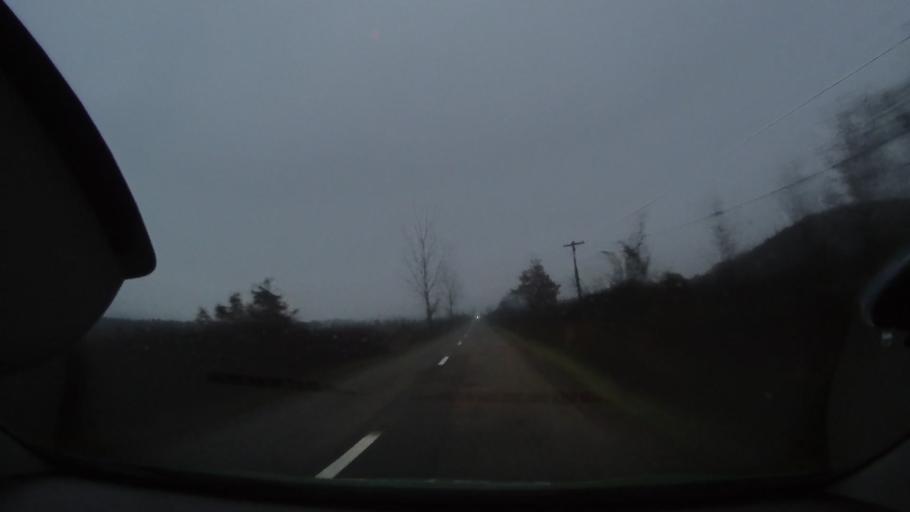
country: RO
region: Arad
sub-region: Comuna Archis
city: Archis
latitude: 46.4776
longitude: 22.0616
